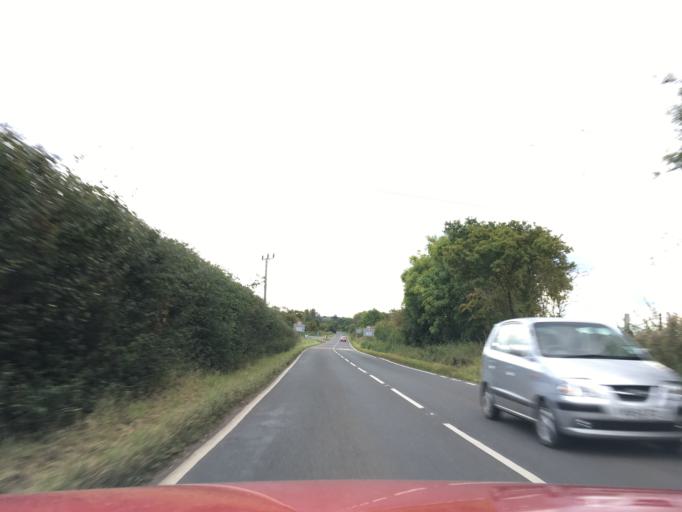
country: GB
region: England
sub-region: South Gloucestershire
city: Tytherington
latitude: 51.5603
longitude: -2.4806
